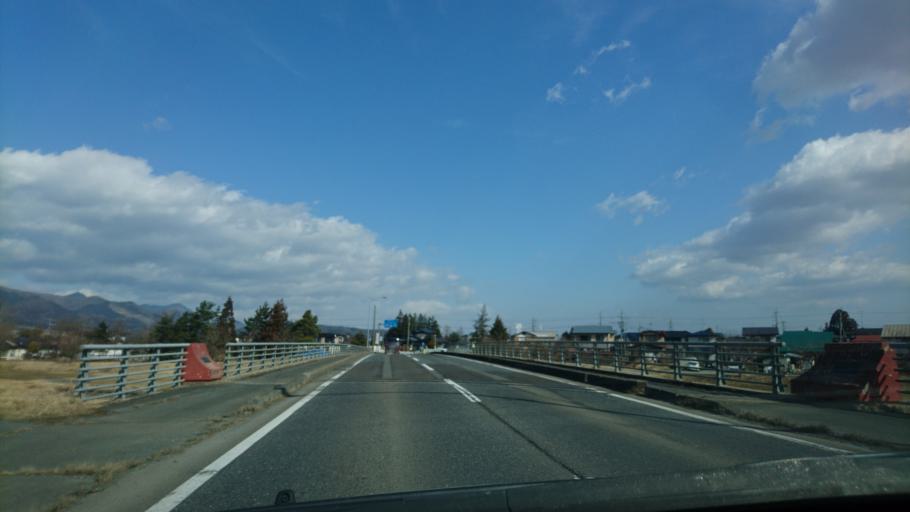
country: JP
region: Iwate
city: Morioka-shi
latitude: 39.5551
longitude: 141.1038
